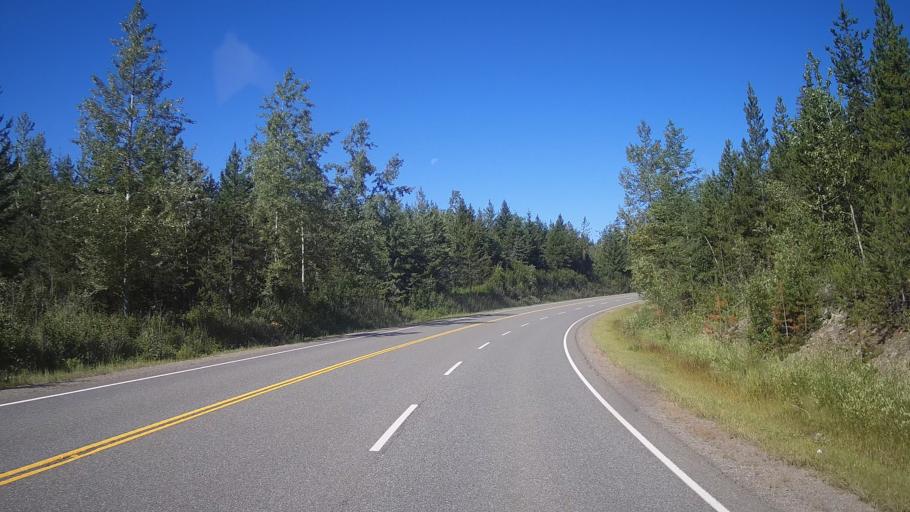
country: CA
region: British Columbia
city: Kamloops
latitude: 51.4869
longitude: -120.3163
